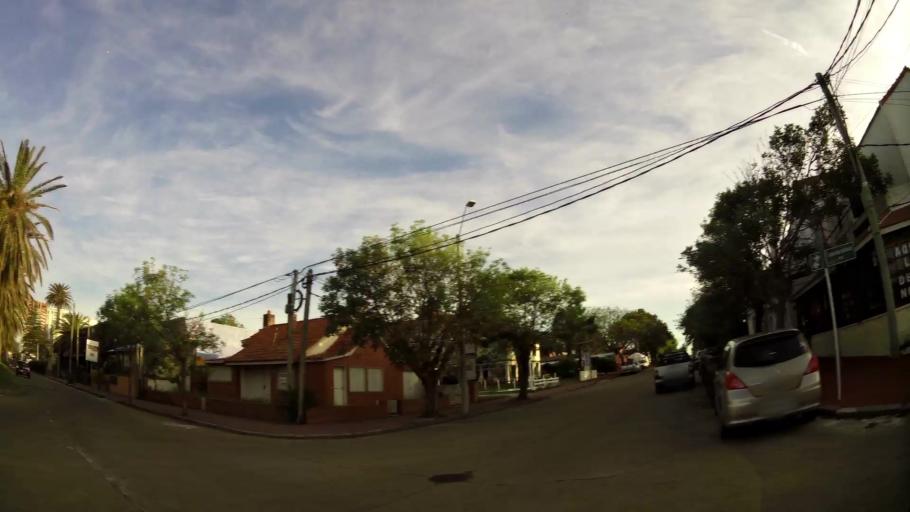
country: UY
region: Maldonado
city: Punta del Este
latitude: -34.9654
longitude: -54.9522
